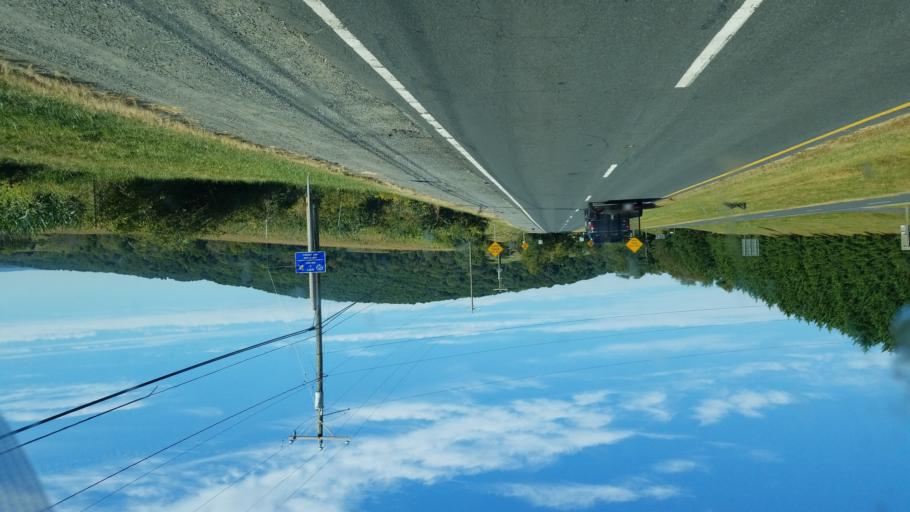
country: US
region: Virginia
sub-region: Warren County
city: Shenandoah Farms
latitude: 39.0031
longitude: -77.9462
